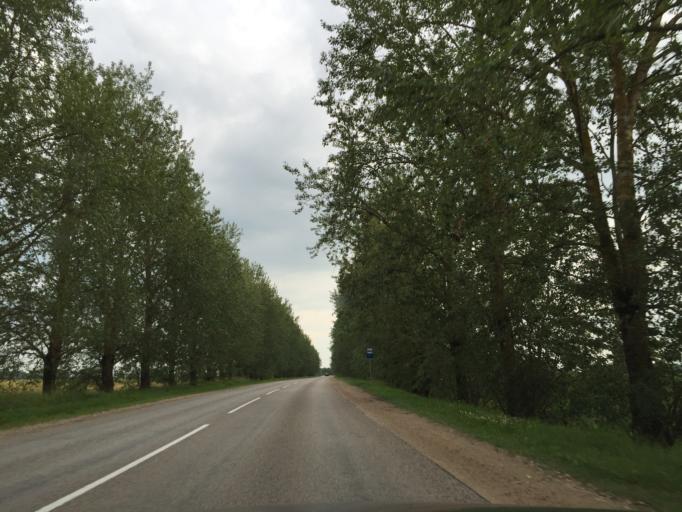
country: LV
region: Dobeles Rajons
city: Dobele
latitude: 56.5800
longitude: 23.2960
